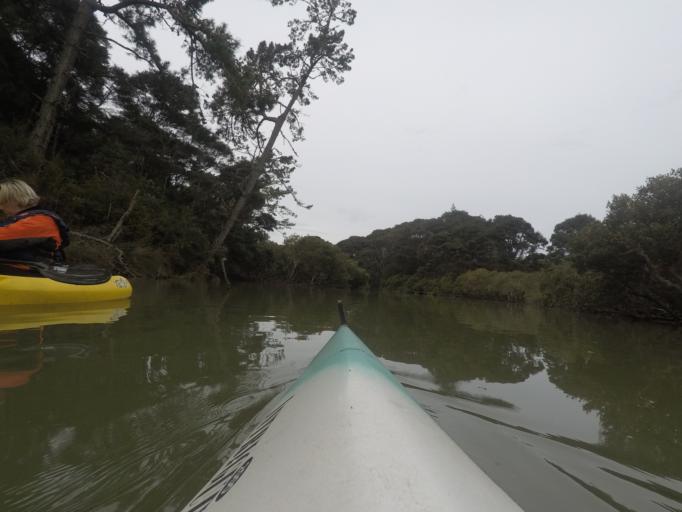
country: NZ
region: Auckland
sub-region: Auckland
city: Rothesay Bay
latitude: -36.6818
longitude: 174.7016
